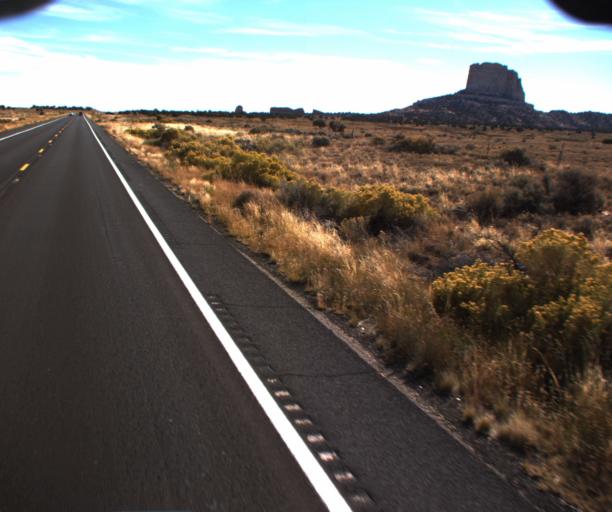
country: US
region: Arizona
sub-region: Coconino County
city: Kaibito
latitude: 36.6160
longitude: -110.9426
